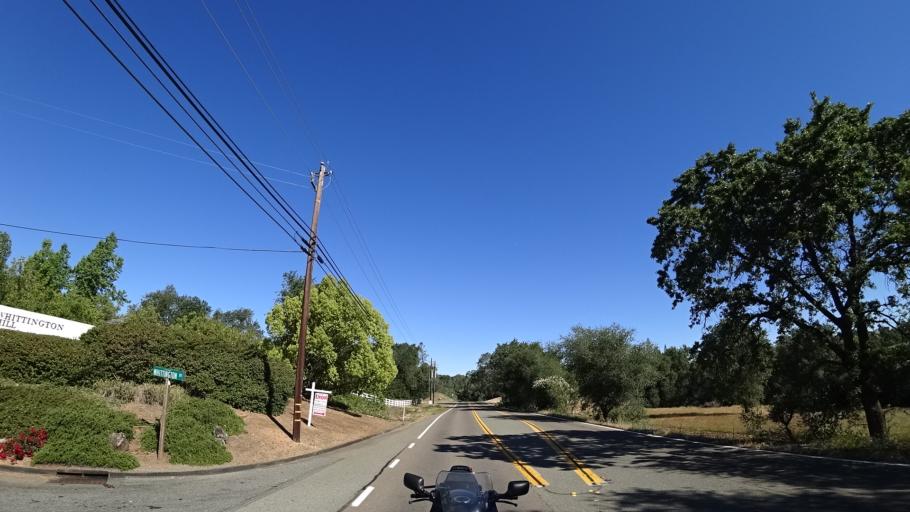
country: US
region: California
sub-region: Placer County
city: Newcastle
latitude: 38.8882
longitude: -121.1775
